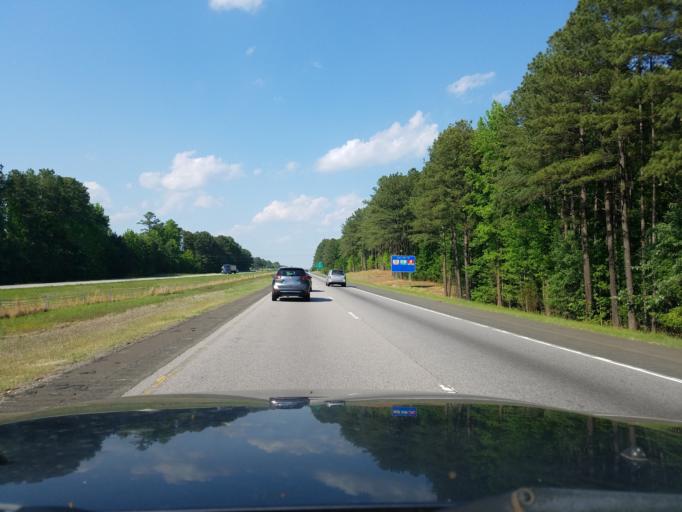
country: US
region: North Carolina
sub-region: Granville County
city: Butner
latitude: 36.1408
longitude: -78.7304
